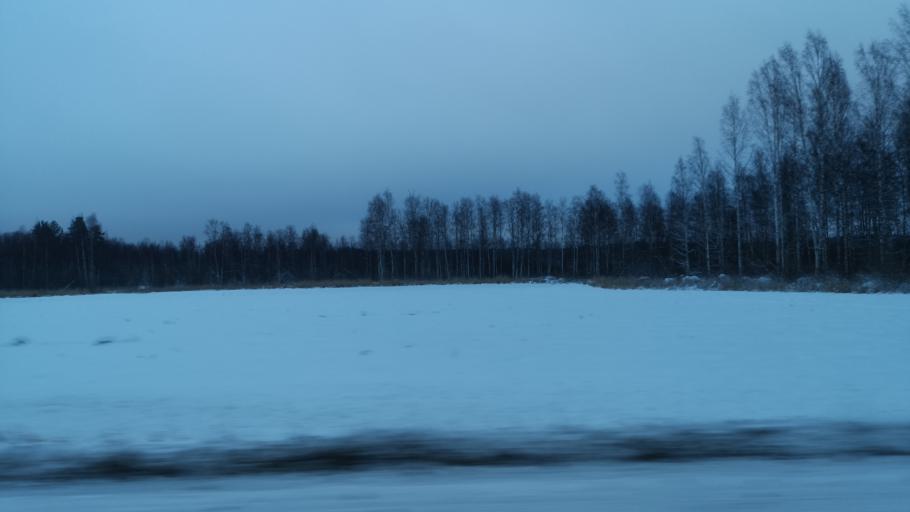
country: FI
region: Southern Savonia
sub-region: Savonlinna
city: Enonkoski
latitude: 62.0828
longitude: 28.6969
